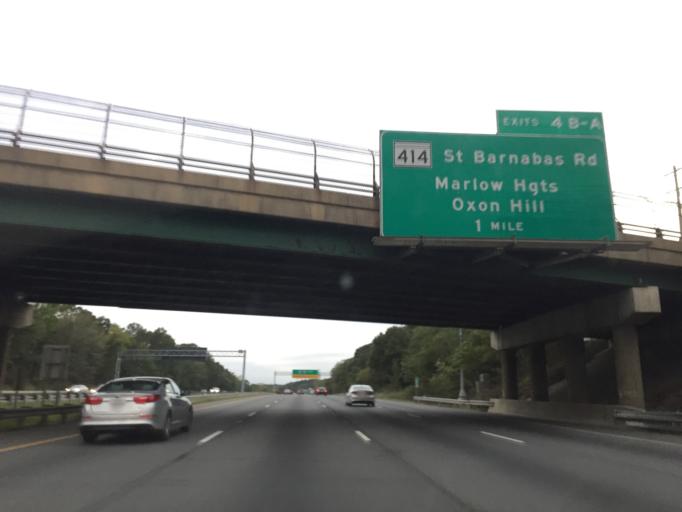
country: US
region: Maryland
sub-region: Prince George's County
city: Temple Hills
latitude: 38.8173
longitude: -76.9486
